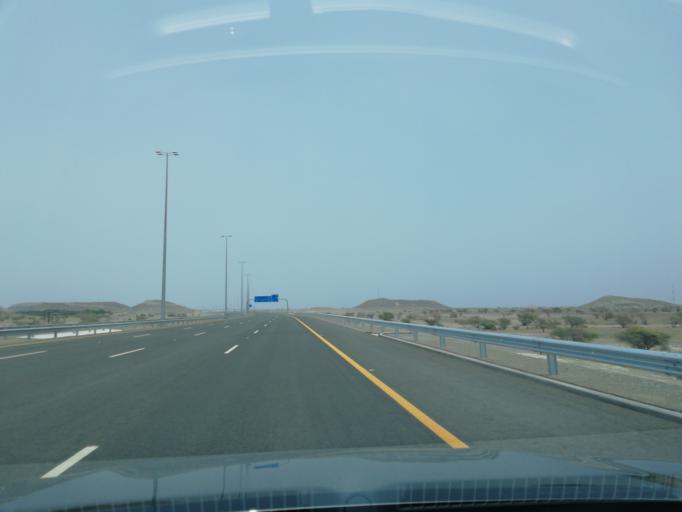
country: OM
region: Al Batinah
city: Al Liwa'
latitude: 24.5121
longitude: 56.5055
